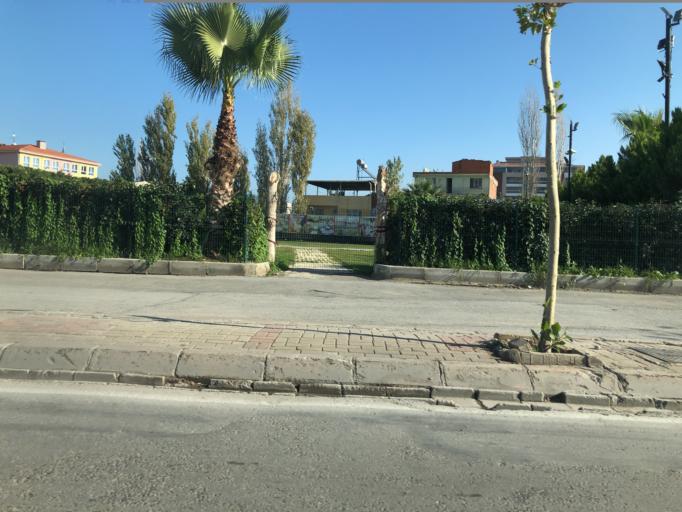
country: TR
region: Izmir
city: Izmir
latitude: 38.4559
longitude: 27.1766
